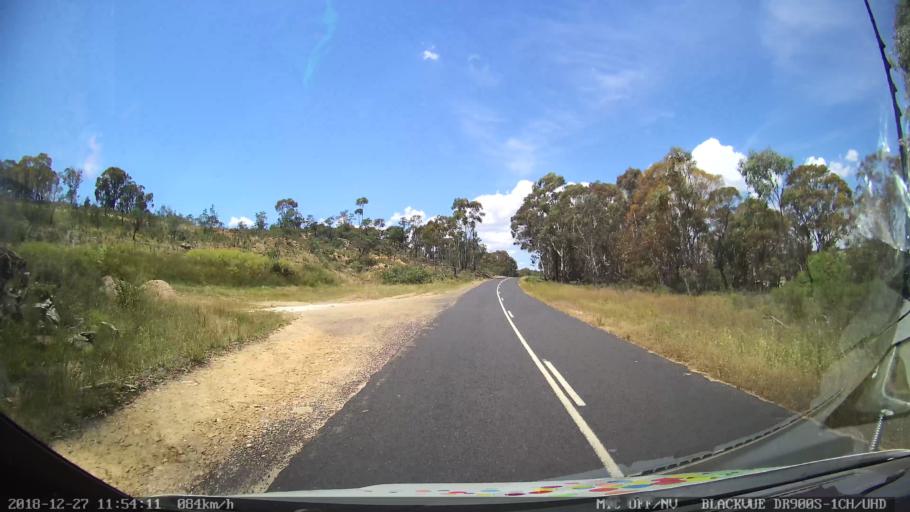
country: AU
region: New South Wales
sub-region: Blayney
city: Blayney
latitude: -33.6717
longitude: 149.4023
